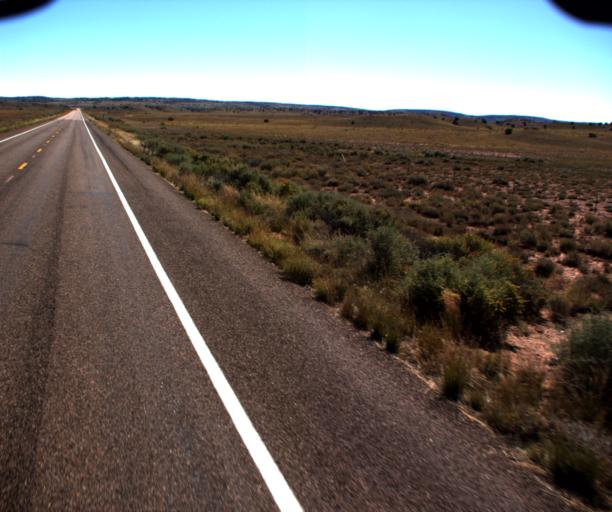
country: US
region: Arizona
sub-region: Apache County
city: Saint Johns
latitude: 34.5920
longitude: -109.6083
